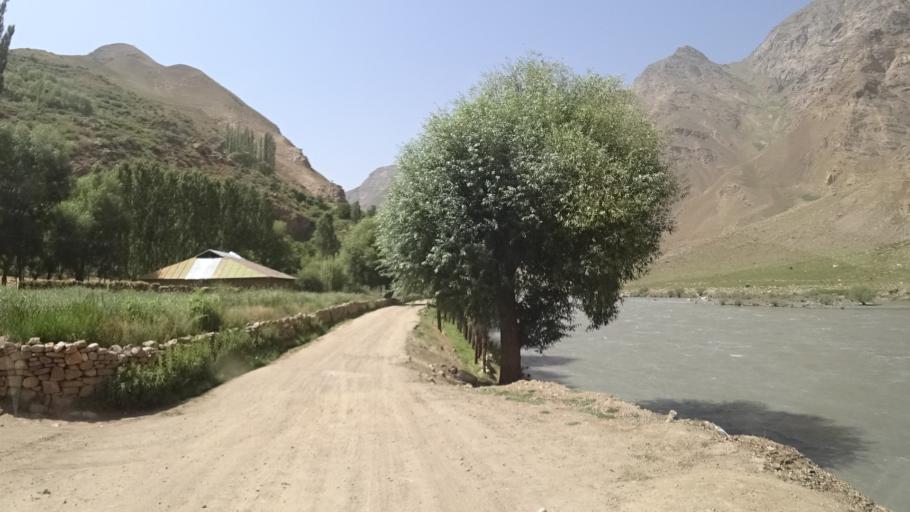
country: TJ
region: Gorno-Badakhshan
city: Khorugh
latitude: 37.1789
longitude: 71.4507
